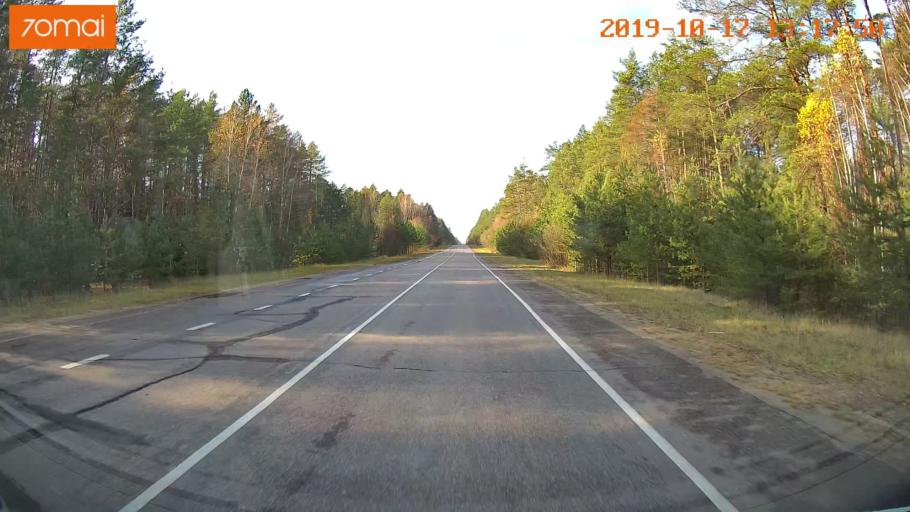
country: RU
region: Rjazan
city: Gus'-Zheleznyy
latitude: 55.0591
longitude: 41.1120
